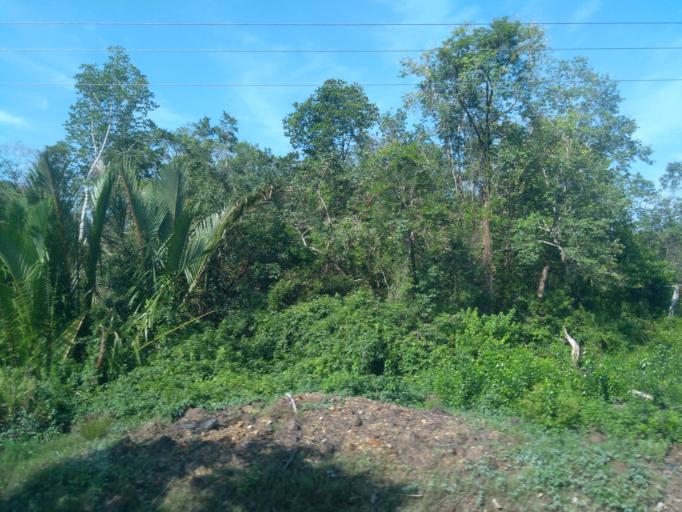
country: MY
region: Sarawak
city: Kuching
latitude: 1.6610
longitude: 110.4325
